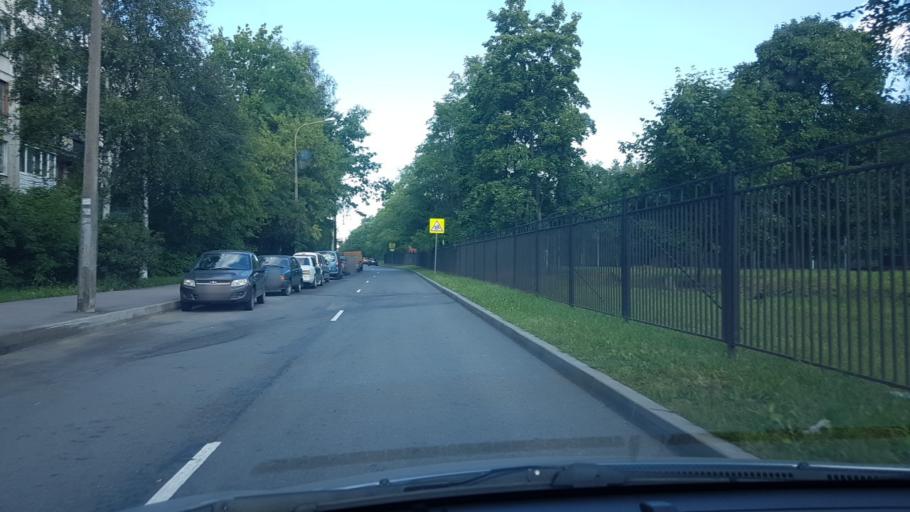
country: RU
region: St.-Petersburg
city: Dachnoye
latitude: 59.8276
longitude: 30.2300
